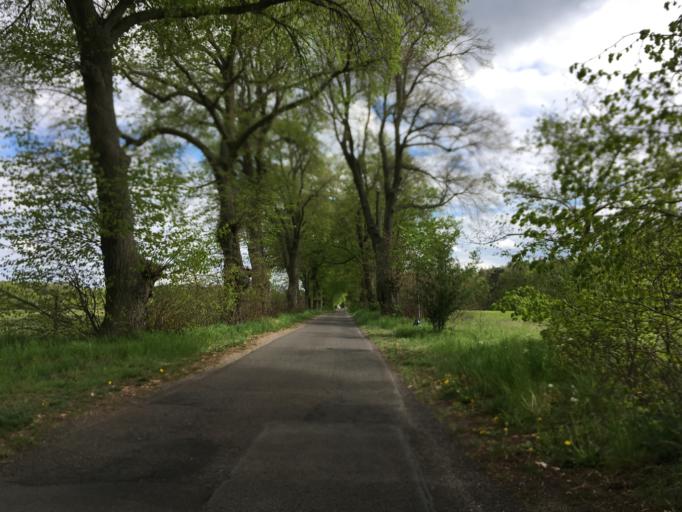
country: DE
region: Brandenburg
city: Rudnitz
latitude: 52.7568
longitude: 13.5824
